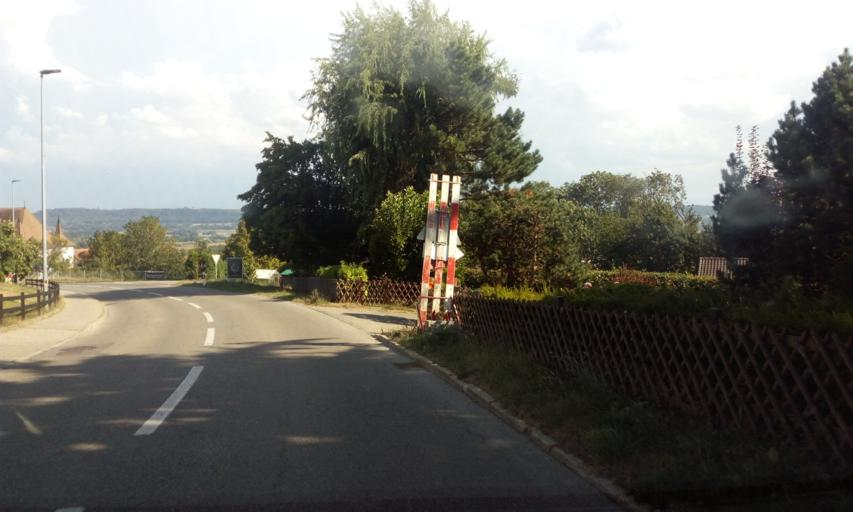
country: CH
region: Fribourg
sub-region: Broye District
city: Domdidier
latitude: 46.8902
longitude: 6.9775
